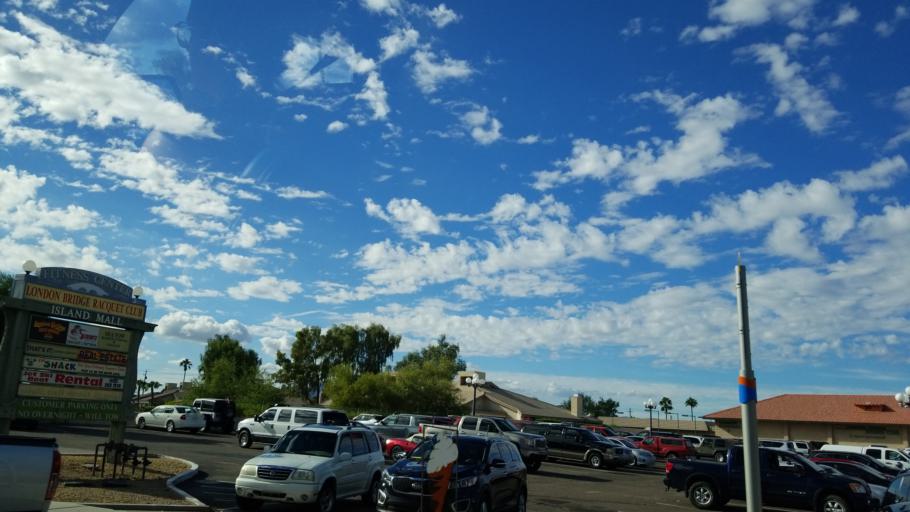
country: US
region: Arizona
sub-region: Mohave County
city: Lake Havasu City
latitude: 34.4705
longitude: -114.3491
